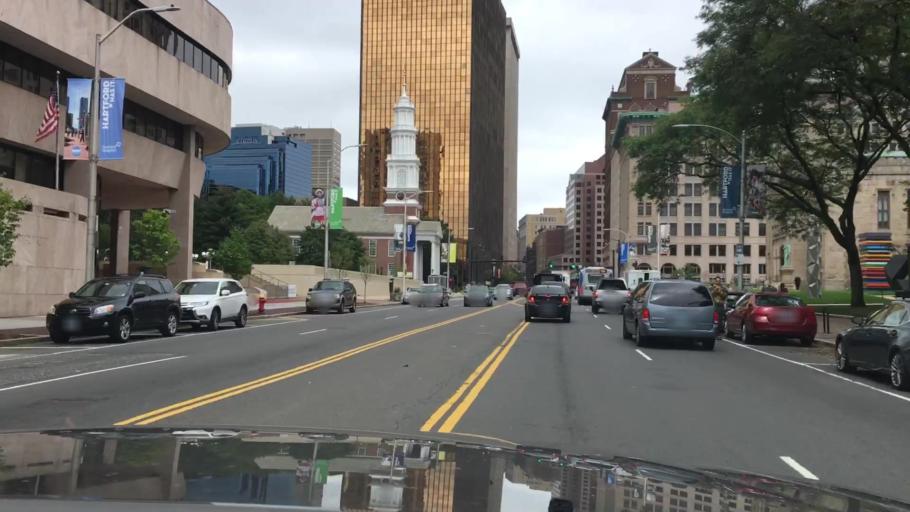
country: US
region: Connecticut
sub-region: Hartford County
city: Hartford
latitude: 41.7628
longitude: -72.6743
